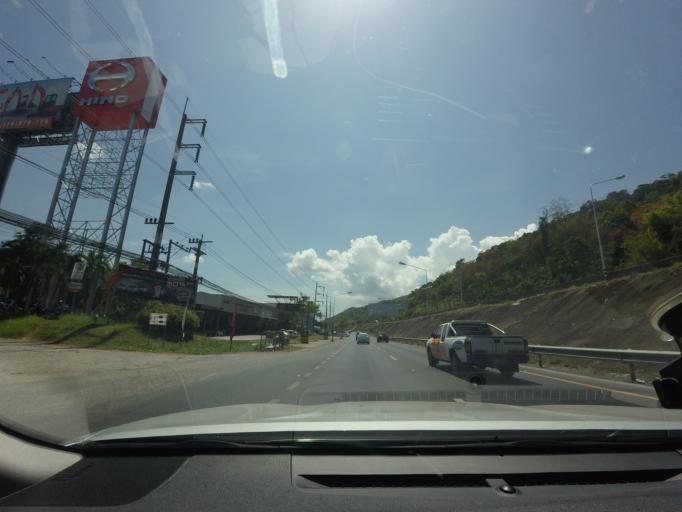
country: TH
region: Phuket
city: Ban Ko Kaeo
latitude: 7.9310
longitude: 98.3747
